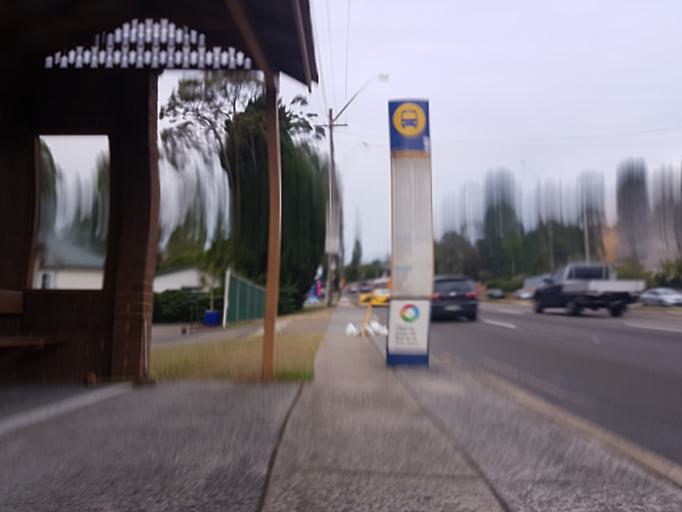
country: AU
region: New South Wales
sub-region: Warringah
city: Forestville
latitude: -33.7626
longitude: 151.2068
